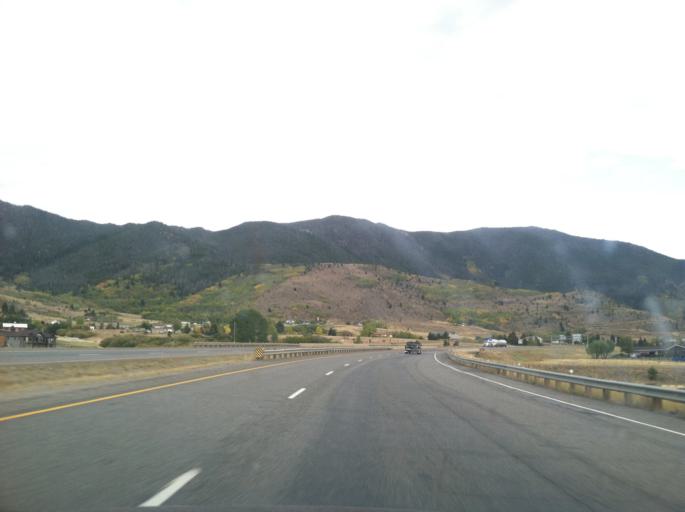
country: US
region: Montana
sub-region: Silver Bow County
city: Butte
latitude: 45.9808
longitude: -112.4822
